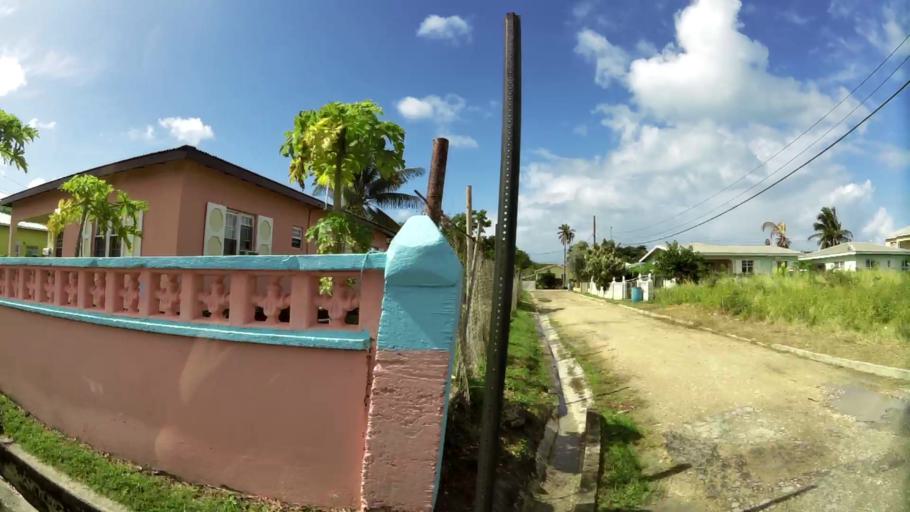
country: AG
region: Saint Mary
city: Bolands
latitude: 17.0679
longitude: -61.8760
